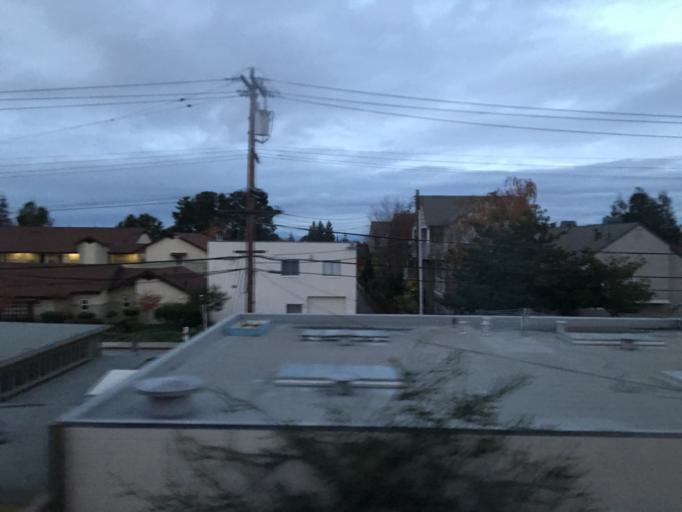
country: US
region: California
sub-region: San Mateo County
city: Belmont
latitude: 37.5221
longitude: -122.2772
